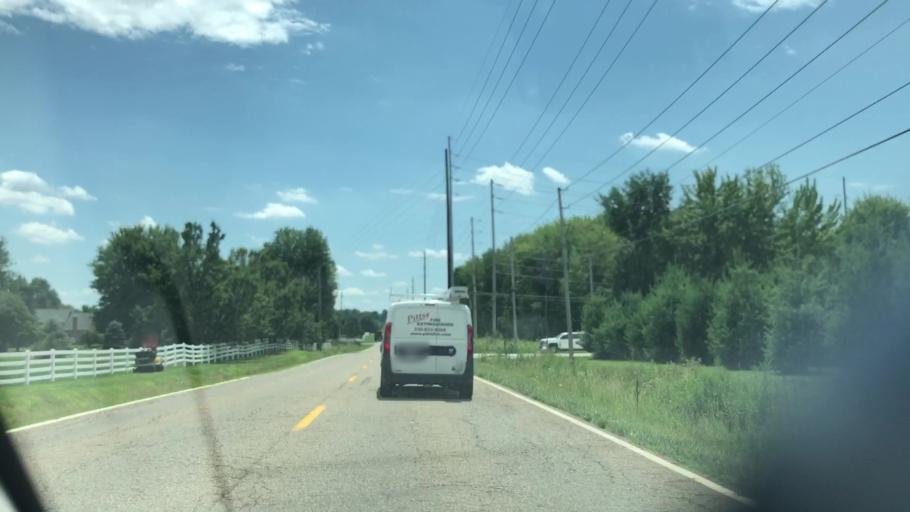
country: US
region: Ohio
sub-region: Summit County
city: Greensburg
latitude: 40.8858
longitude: -81.4991
